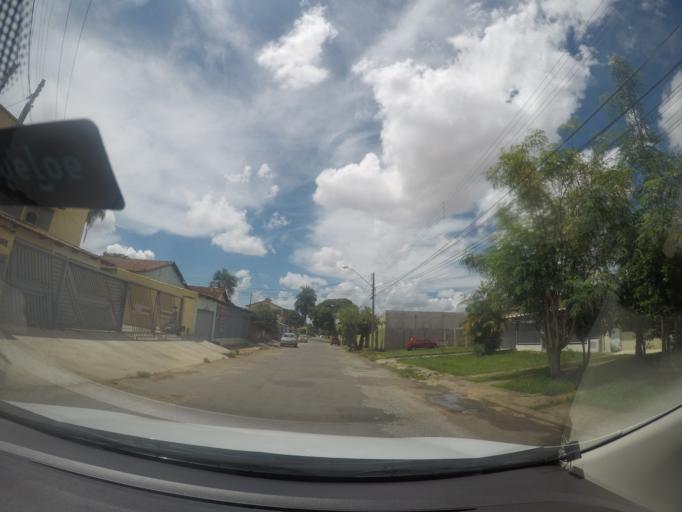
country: BR
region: Goias
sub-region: Goiania
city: Goiania
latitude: -16.6829
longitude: -49.3181
